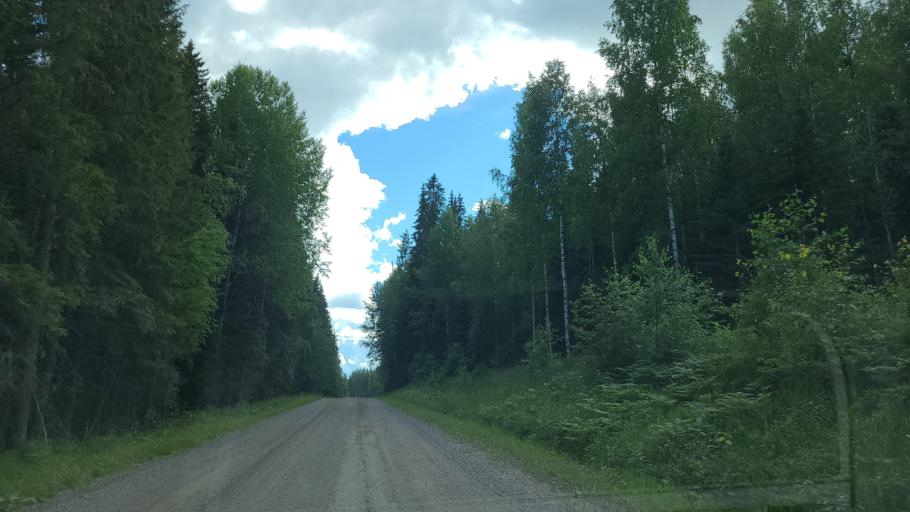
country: FI
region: Central Finland
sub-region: Jaemsae
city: Jaemsae
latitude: 61.9205
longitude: 25.3100
